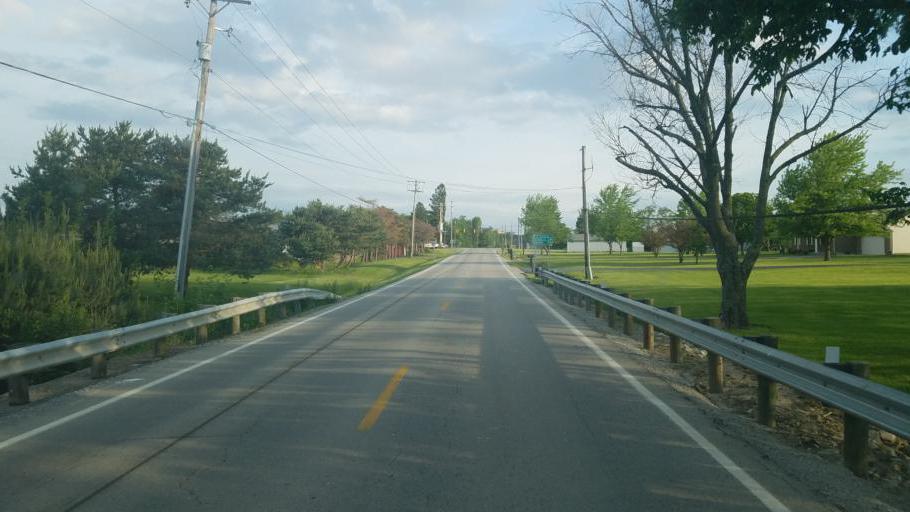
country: US
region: Ohio
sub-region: Clinton County
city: Sabina
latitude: 39.4739
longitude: -83.6711
